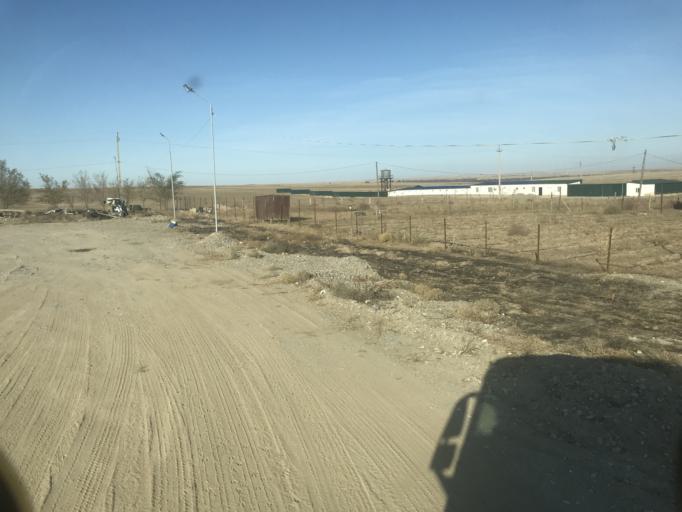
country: KZ
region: Ongtustik Qazaqstan
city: Temirlanovka
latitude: 42.5693
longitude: 69.3121
